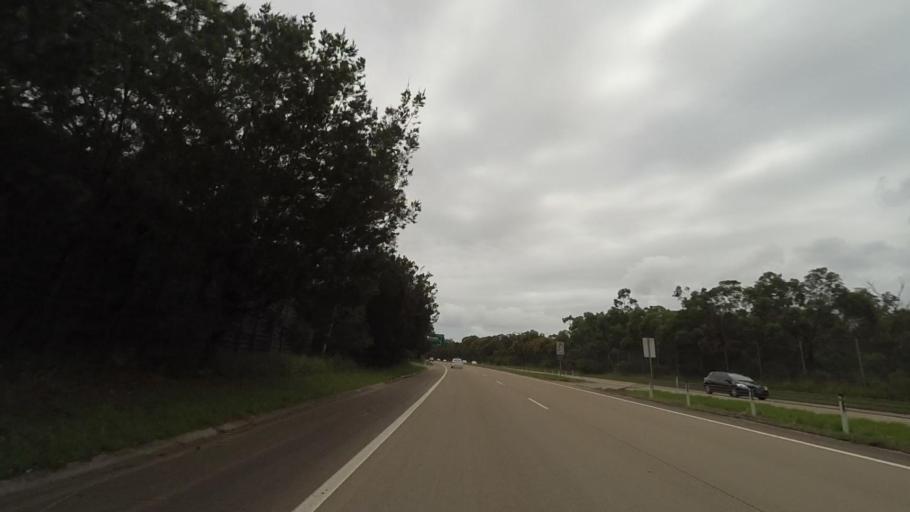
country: AU
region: New South Wales
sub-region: Lake Macquarie Shire
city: Cardiff South
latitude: -32.9662
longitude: 151.6758
